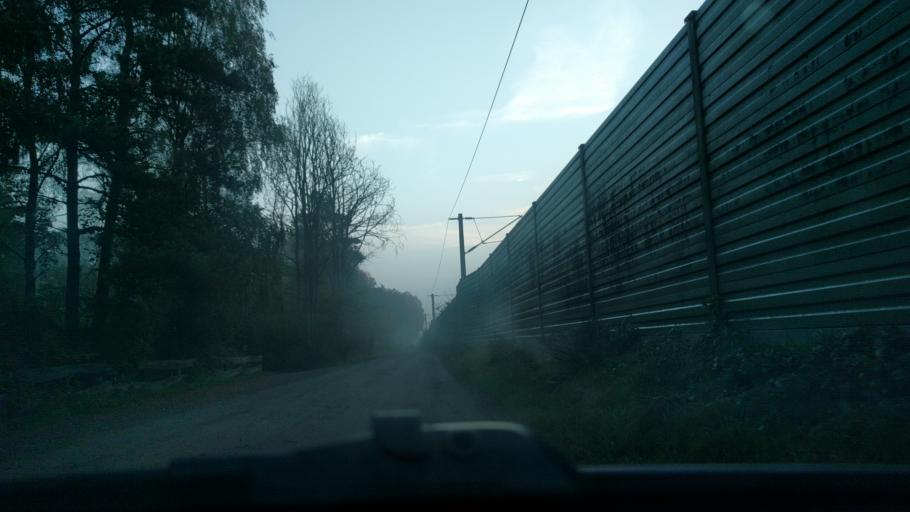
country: DE
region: Lower Saxony
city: Ribbesbuttel
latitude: 52.4567
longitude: 10.4947
